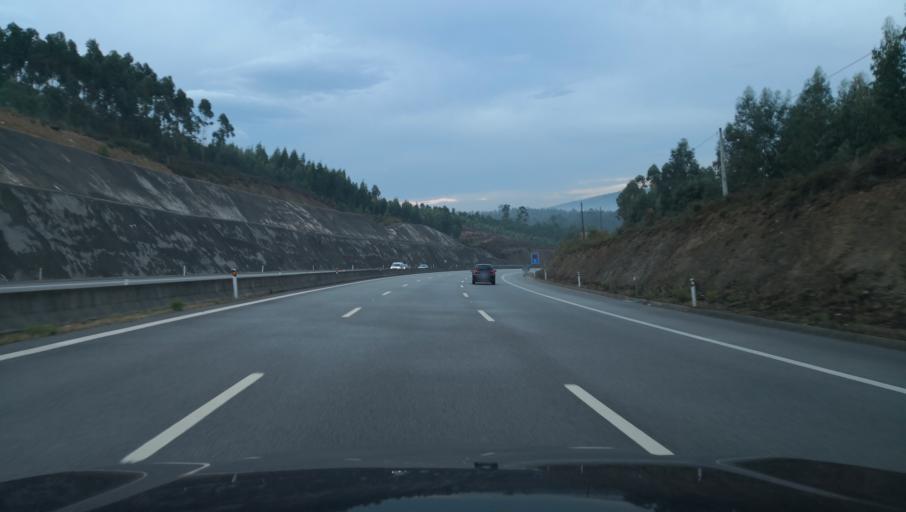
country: PT
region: Porto
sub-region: Paredes
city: Recarei
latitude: 41.1138
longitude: -8.4321
